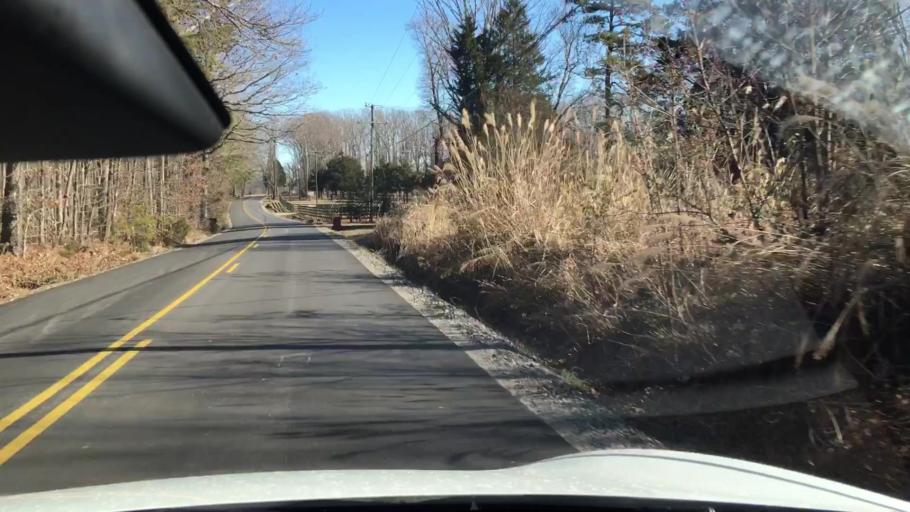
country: US
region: Virginia
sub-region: Powhatan County
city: Powhatan
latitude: 37.5636
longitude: -77.7908
